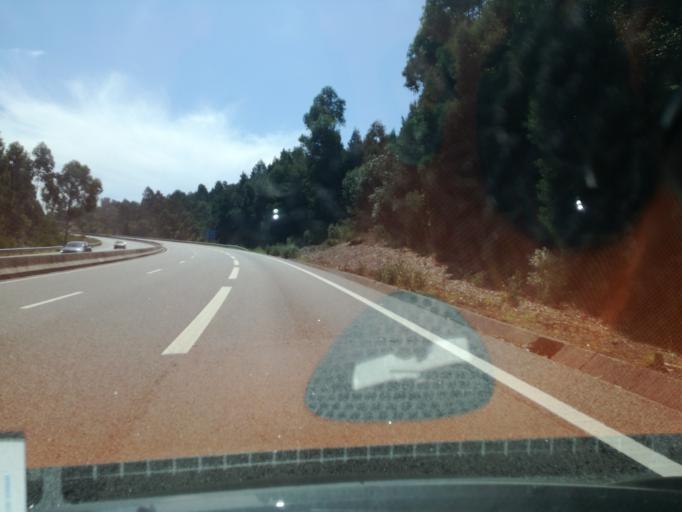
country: PT
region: Viana do Castelo
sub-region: Caminha
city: Vila Praia de Ancora
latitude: 41.7806
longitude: -8.7885
